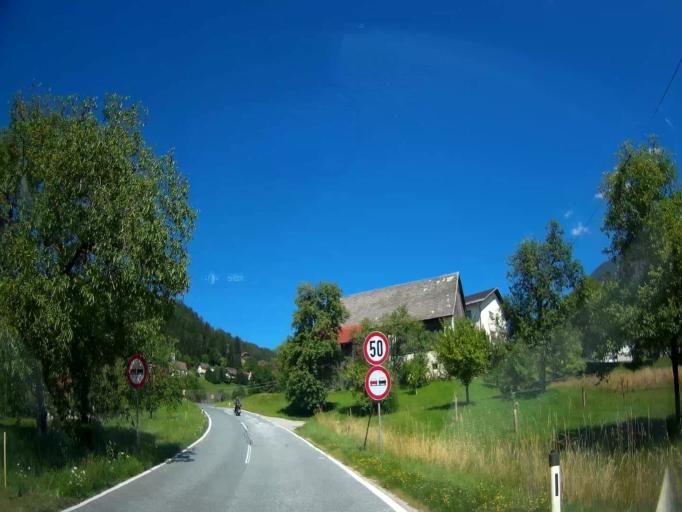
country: AT
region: Carinthia
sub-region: Politischer Bezirk Klagenfurt Land
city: Grafenstein
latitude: 46.5388
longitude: 14.4442
